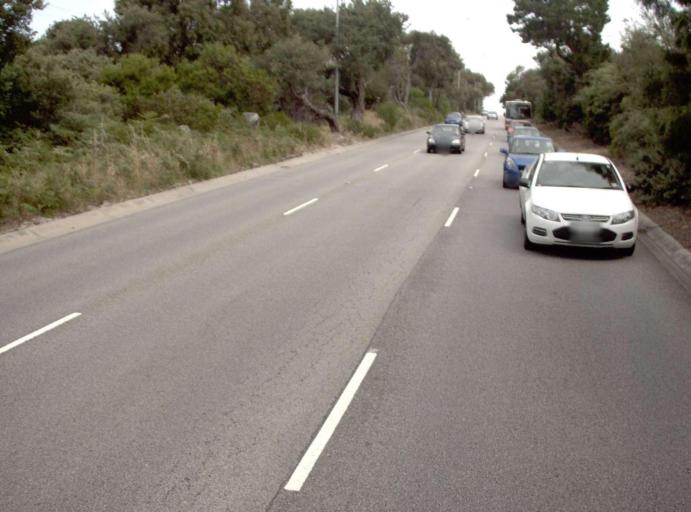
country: AU
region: Victoria
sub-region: Frankston
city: Frankston South
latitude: -38.1589
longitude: 145.1351
